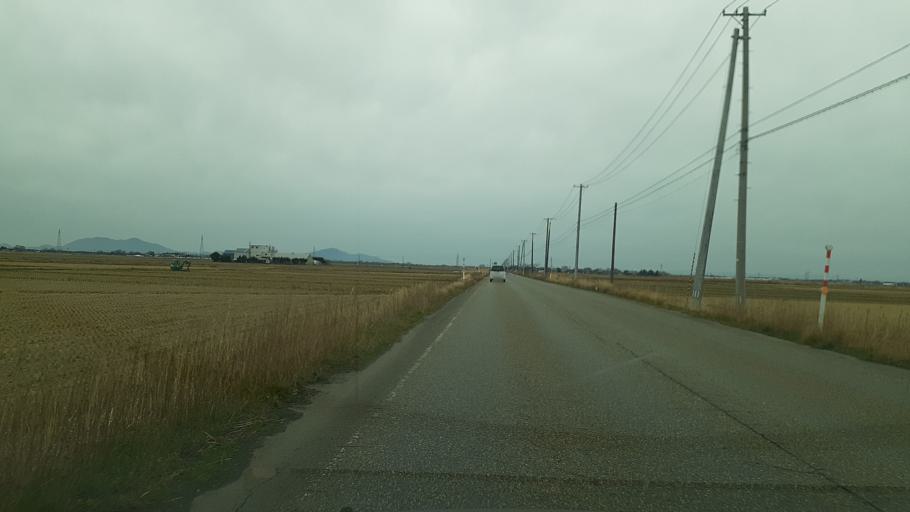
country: JP
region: Niigata
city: Niitsu-honcho
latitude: 37.8158
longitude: 139.0922
